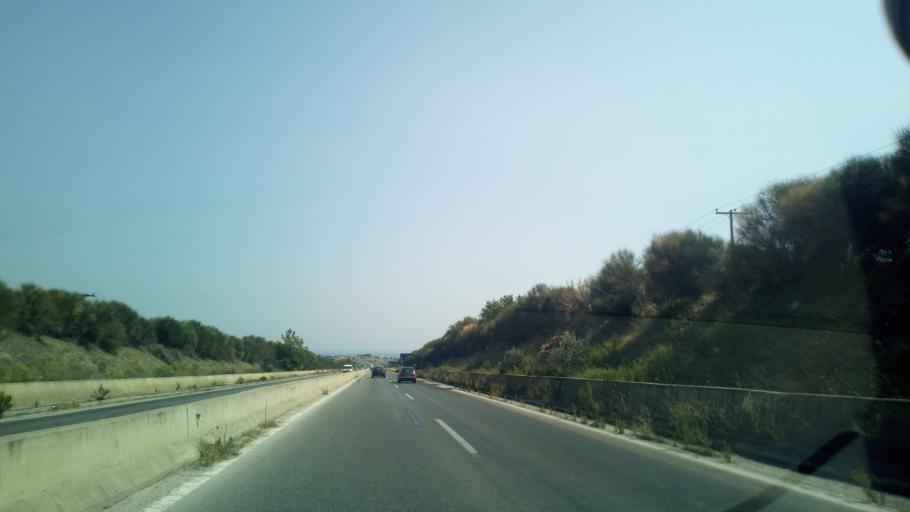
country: GR
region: Central Macedonia
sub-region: Nomos Chalkidikis
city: Nea Triglia
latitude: 40.2947
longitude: 23.1408
